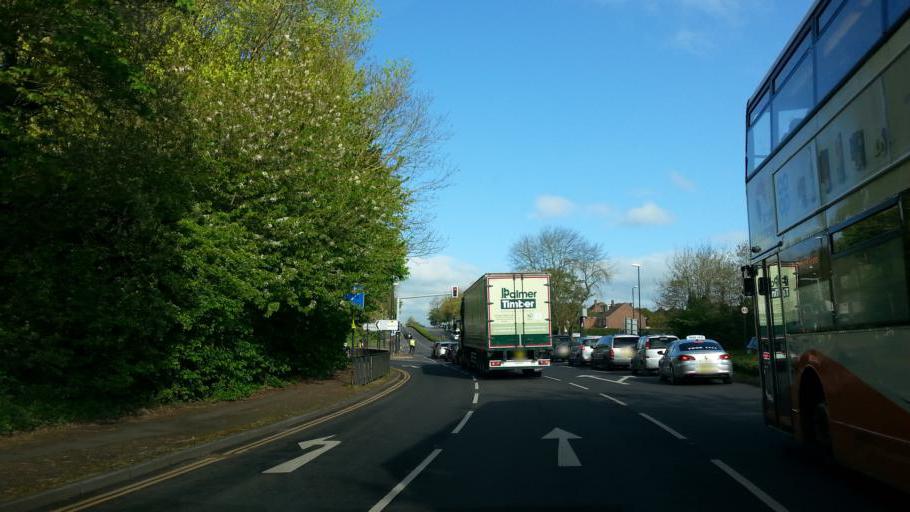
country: GB
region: England
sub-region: Warwickshire
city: Ryton on Dunsmore
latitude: 52.4041
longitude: -1.4591
